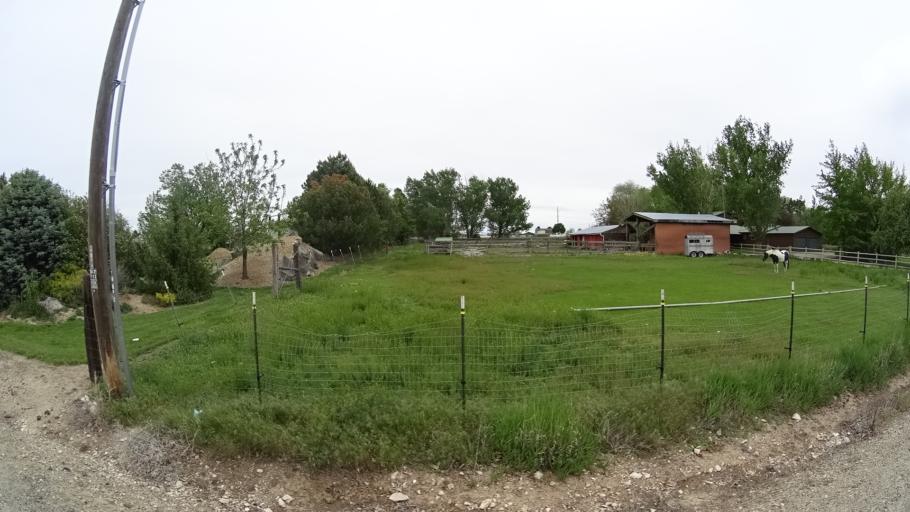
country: US
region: Idaho
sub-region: Ada County
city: Kuna
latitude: 43.4953
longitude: -116.3394
